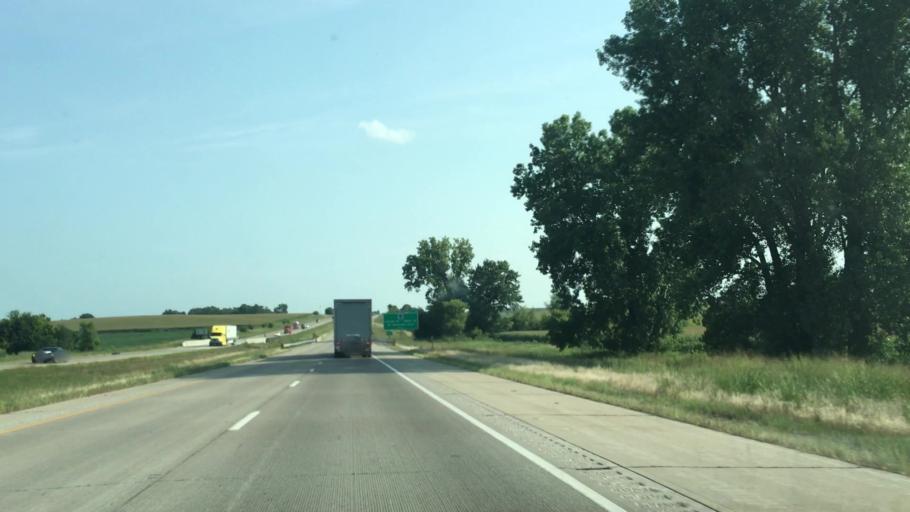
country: US
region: Iowa
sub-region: Scott County
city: Walcott
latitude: 41.5575
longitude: -90.6786
